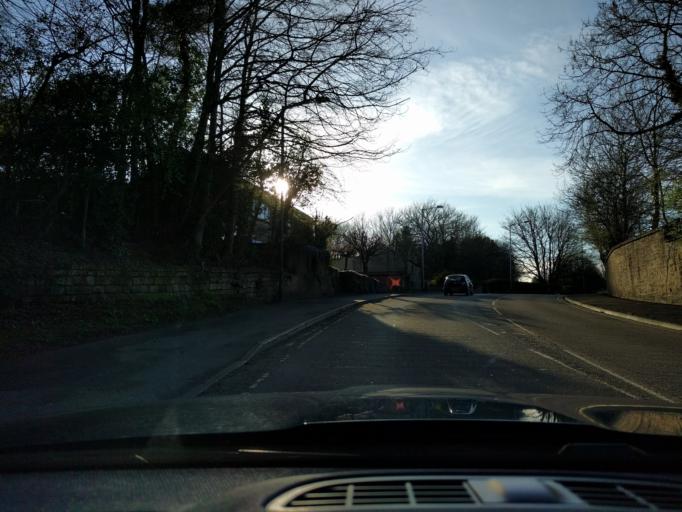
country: GB
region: England
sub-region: Northumberland
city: Morpeth
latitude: 55.1734
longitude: -1.6986
